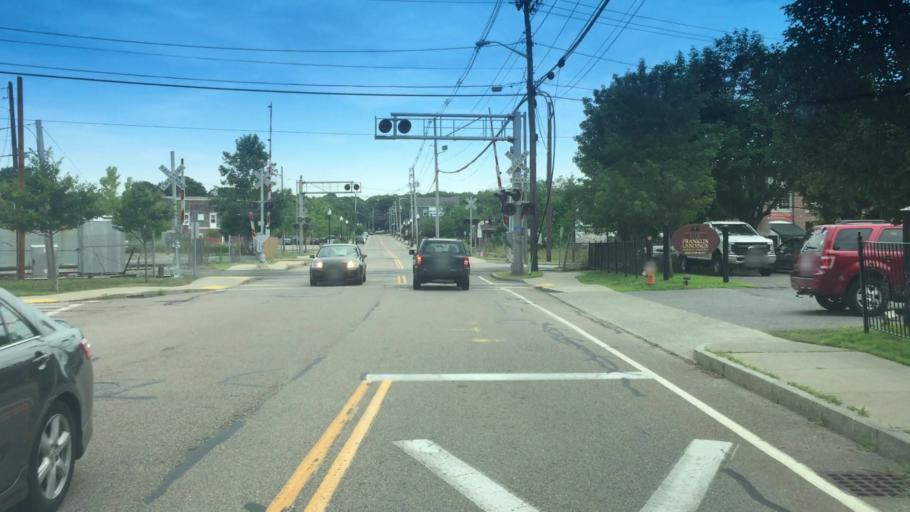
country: US
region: Massachusetts
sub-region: Norfolk County
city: Franklin
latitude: 42.0789
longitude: -71.4037
